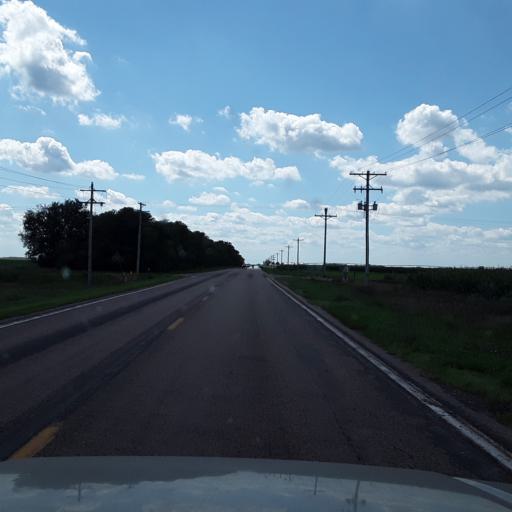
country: US
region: Nebraska
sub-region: Merrick County
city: Central City
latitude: 41.1910
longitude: -98.0201
